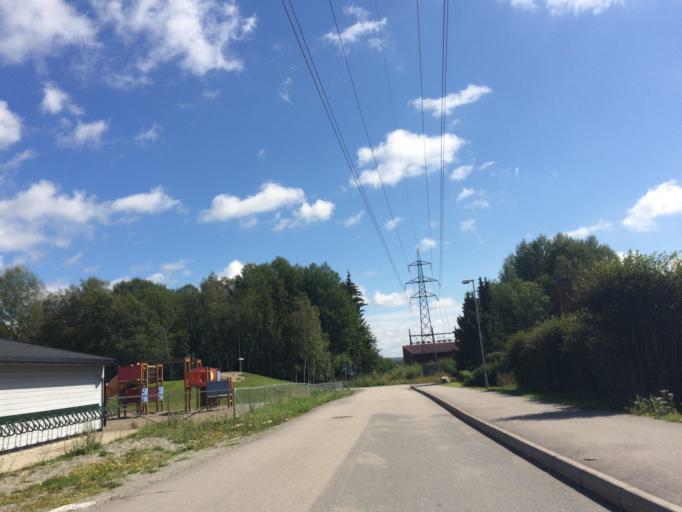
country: NO
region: Akershus
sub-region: Ski
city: Ski
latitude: 59.7150
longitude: 10.8210
